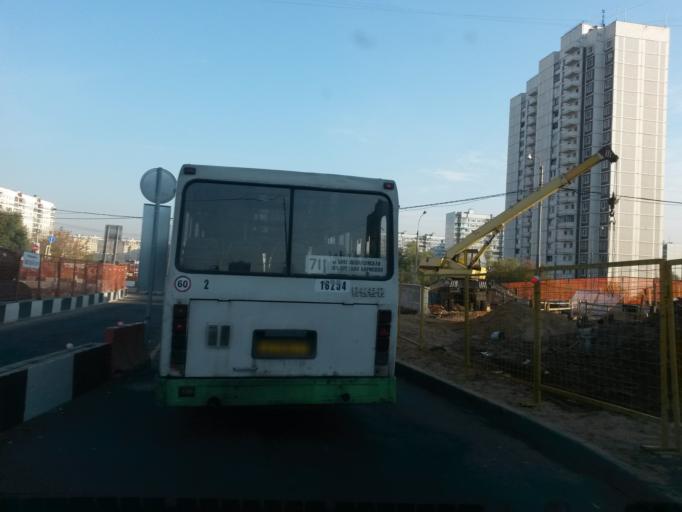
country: RU
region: Moscow
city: Orekhovo-Borisovo
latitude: 55.6262
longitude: 37.7425
